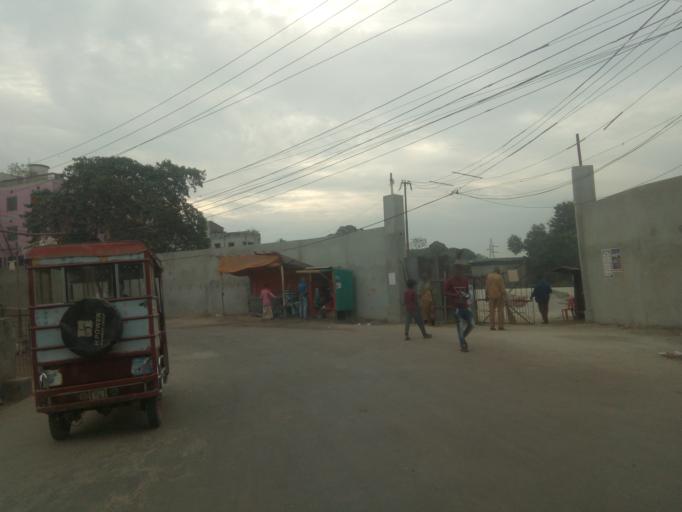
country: BD
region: Dhaka
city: Narayanganj
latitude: 23.6010
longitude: 90.5020
